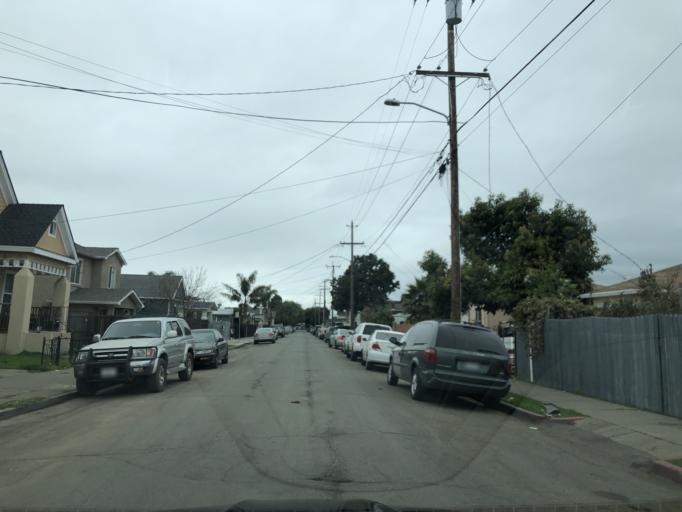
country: US
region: California
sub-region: Alameda County
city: San Leandro
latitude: 37.7434
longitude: -122.1779
